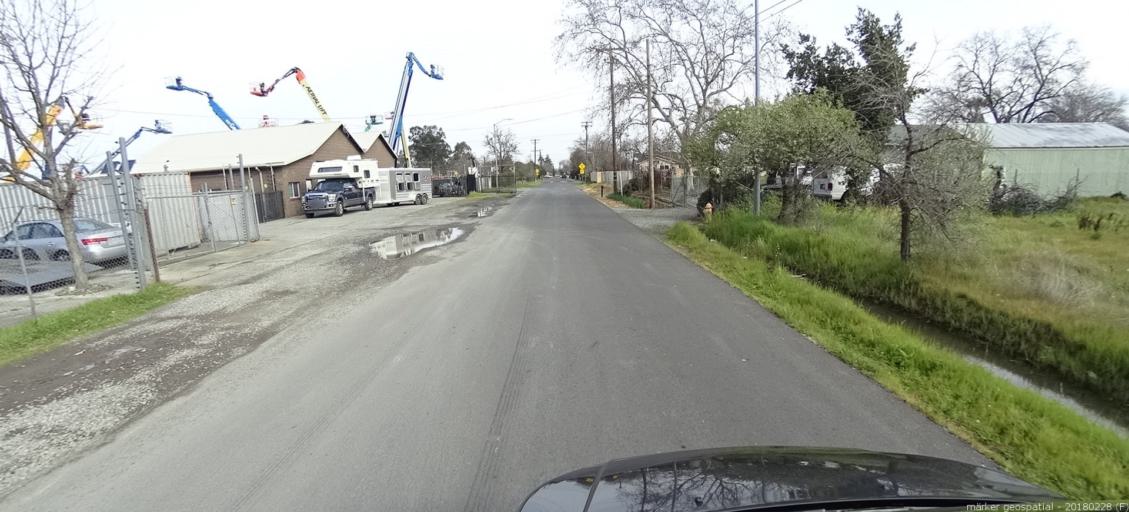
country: US
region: California
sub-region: Sacramento County
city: Rio Linda
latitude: 38.6936
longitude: -121.4500
